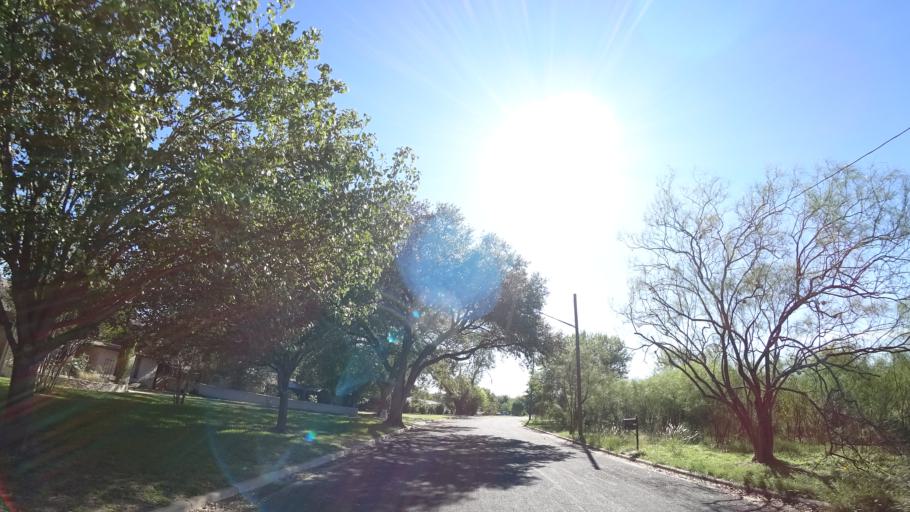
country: US
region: Texas
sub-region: Travis County
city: Austin
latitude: 30.2293
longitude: -97.7095
